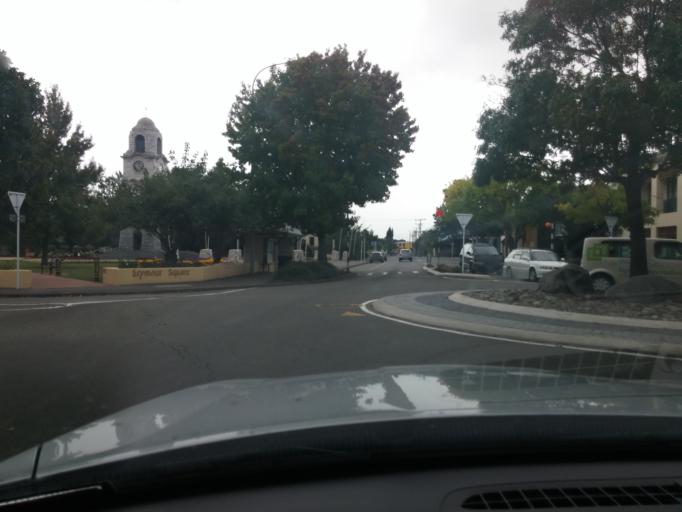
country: NZ
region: Marlborough
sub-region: Marlborough District
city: Blenheim
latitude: -41.5120
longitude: 173.9545
